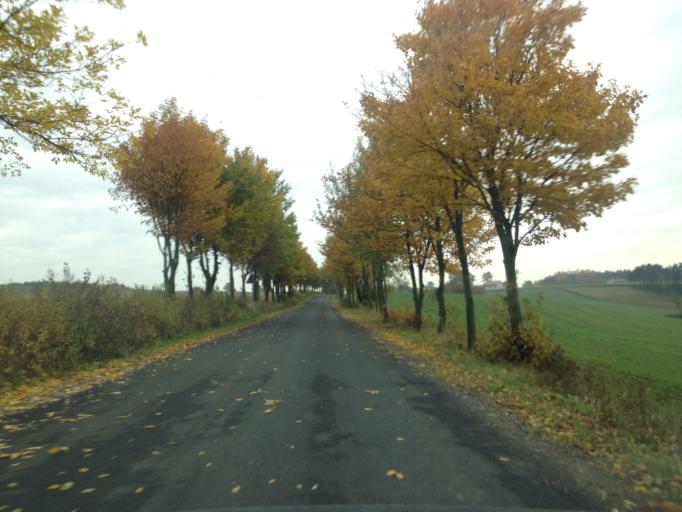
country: PL
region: Kujawsko-Pomorskie
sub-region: Powiat brodnicki
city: Brzozie
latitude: 53.2953
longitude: 19.6971
